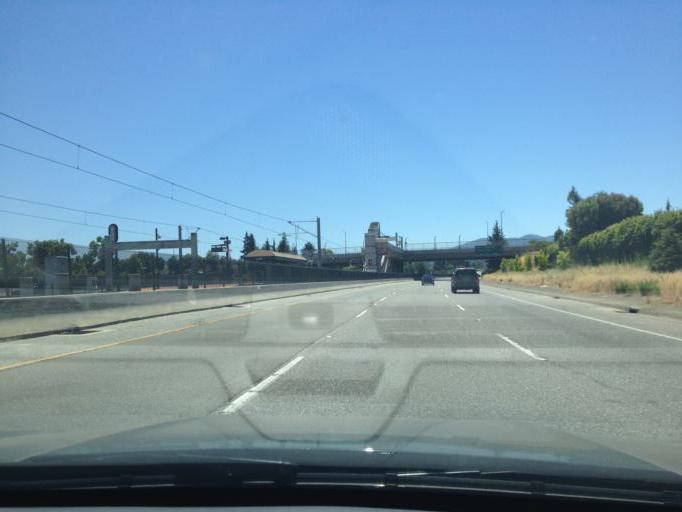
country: US
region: California
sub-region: Santa Clara County
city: Seven Trees
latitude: 37.2678
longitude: -121.8598
